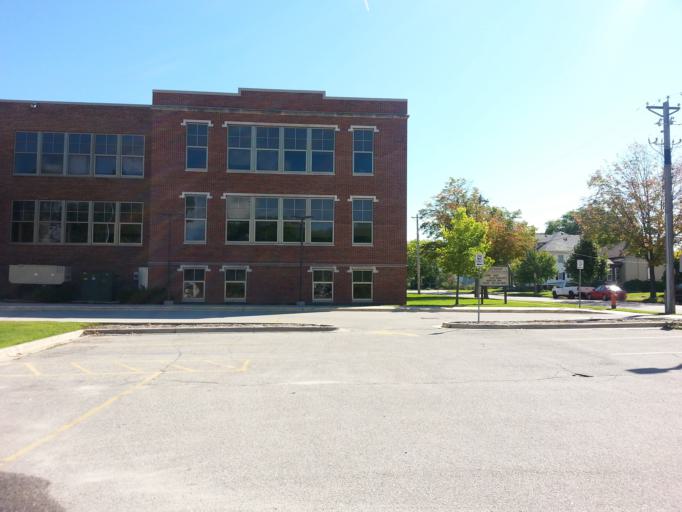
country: US
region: Minnesota
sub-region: Olmsted County
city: Rochester
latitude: 44.0316
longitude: -92.4673
